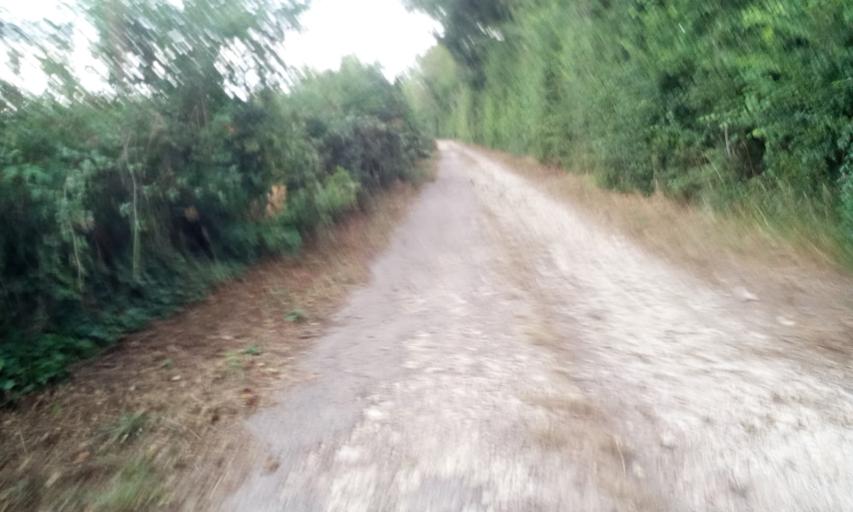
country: FR
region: Lower Normandy
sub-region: Departement du Calvados
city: Troarn
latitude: 49.1847
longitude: -0.2012
